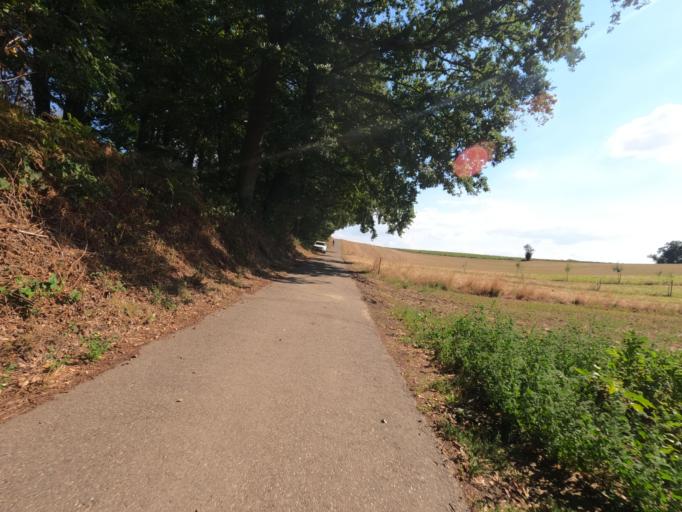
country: DE
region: North Rhine-Westphalia
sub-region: Regierungsbezirk Koln
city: Wassenberg
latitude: 51.0918
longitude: 6.1859
